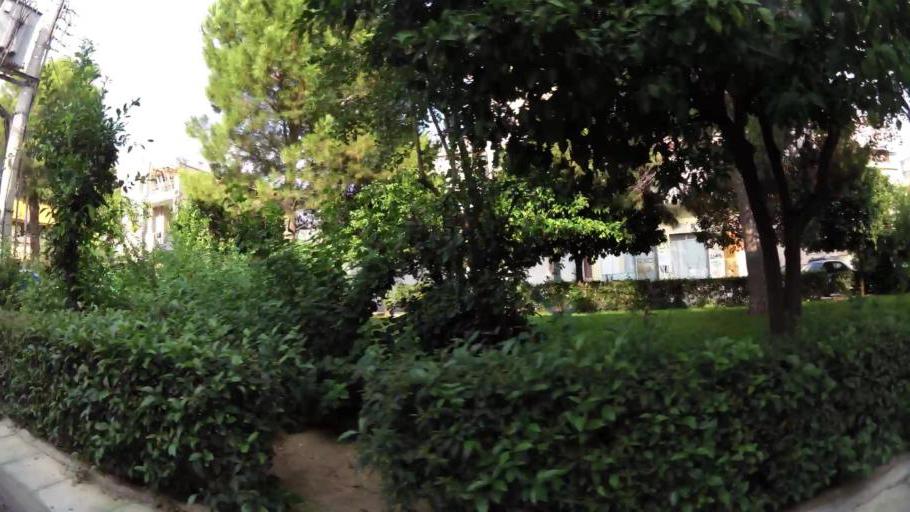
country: GR
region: Attica
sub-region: Nomarchia Athinas
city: Petroupolis
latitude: 38.0425
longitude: 23.6921
